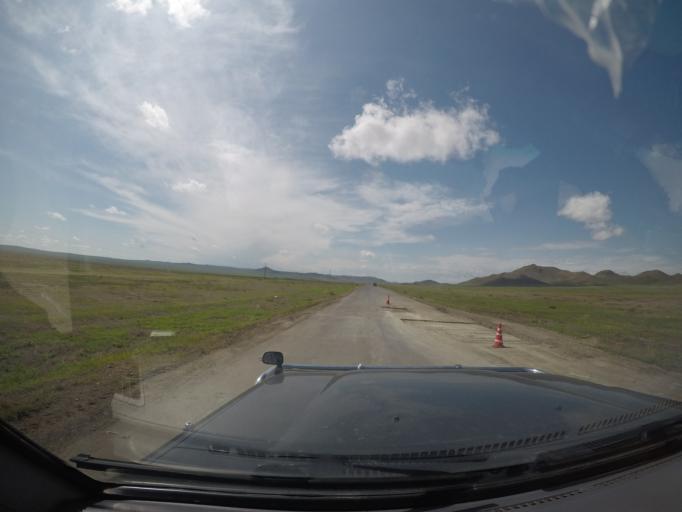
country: MN
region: Hentiy
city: Moron
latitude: 47.3791
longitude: 110.4129
